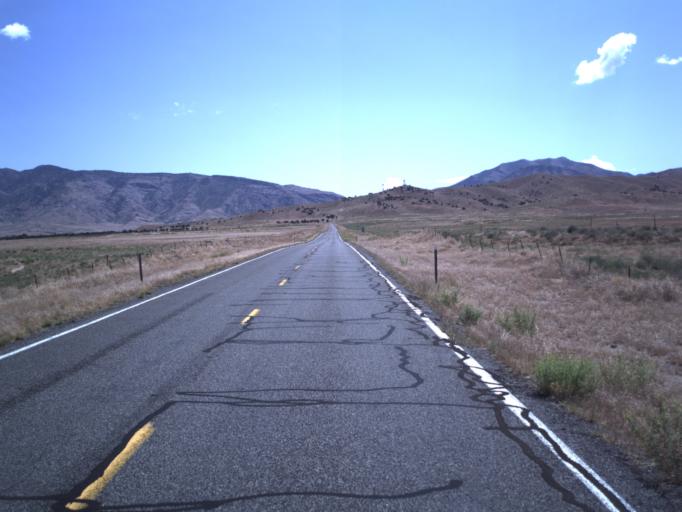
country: US
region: Utah
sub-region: Millard County
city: Delta
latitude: 39.3548
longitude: -112.3817
